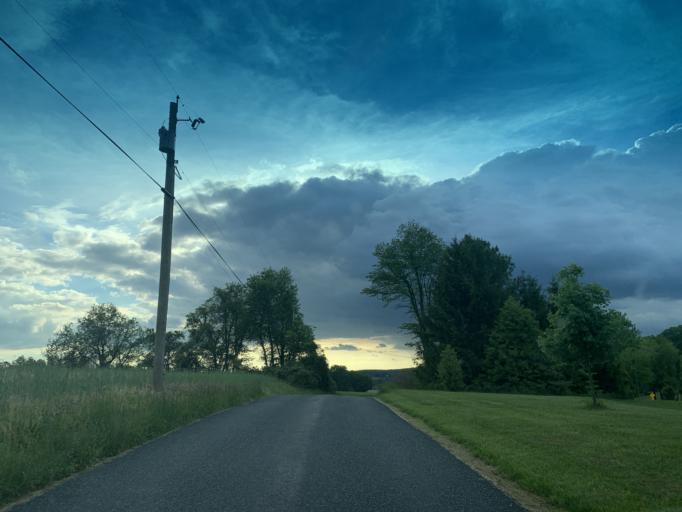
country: US
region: Pennsylvania
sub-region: York County
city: Susquehanna Trails
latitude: 39.6728
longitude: -76.2665
